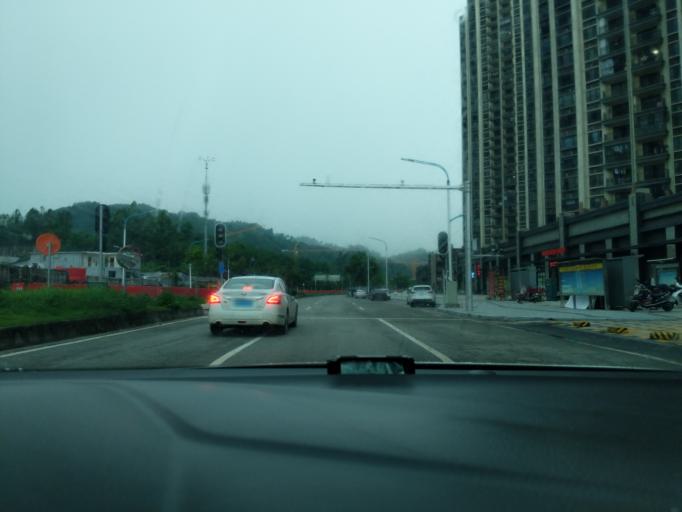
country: CN
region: Guangdong
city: Huangge
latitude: 22.7984
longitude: 113.5143
